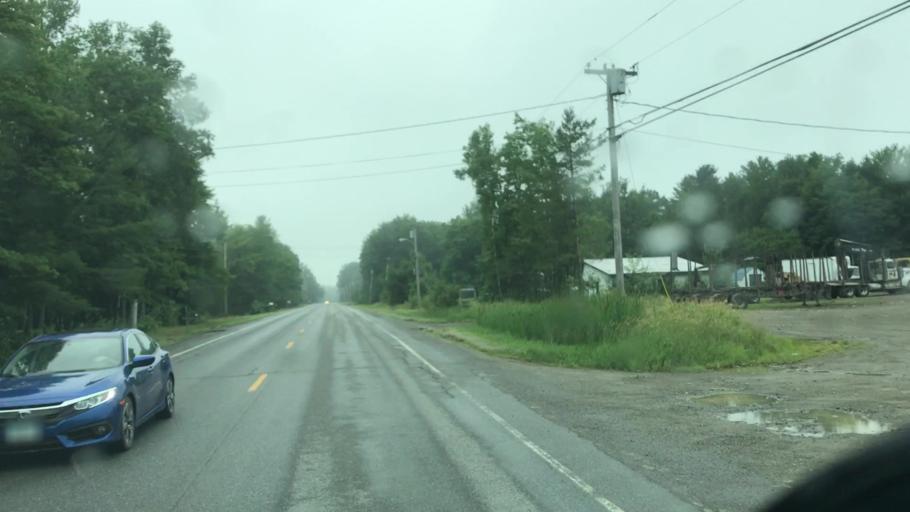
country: US
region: Maine
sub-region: Penobscot County
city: Howland
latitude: 45.2655
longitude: -68.6386
